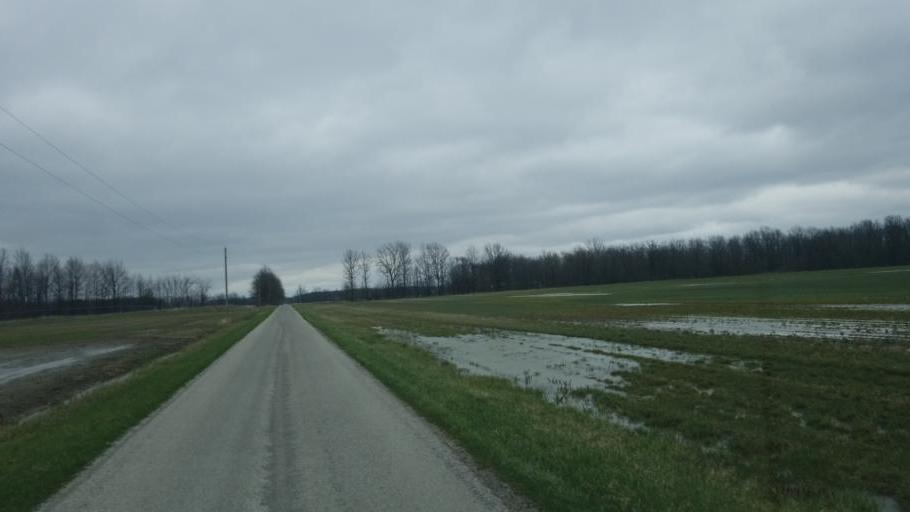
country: US
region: Ohio
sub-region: Wyandot County
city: Upper Sandusky
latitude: 40.6873
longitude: -83.3607
